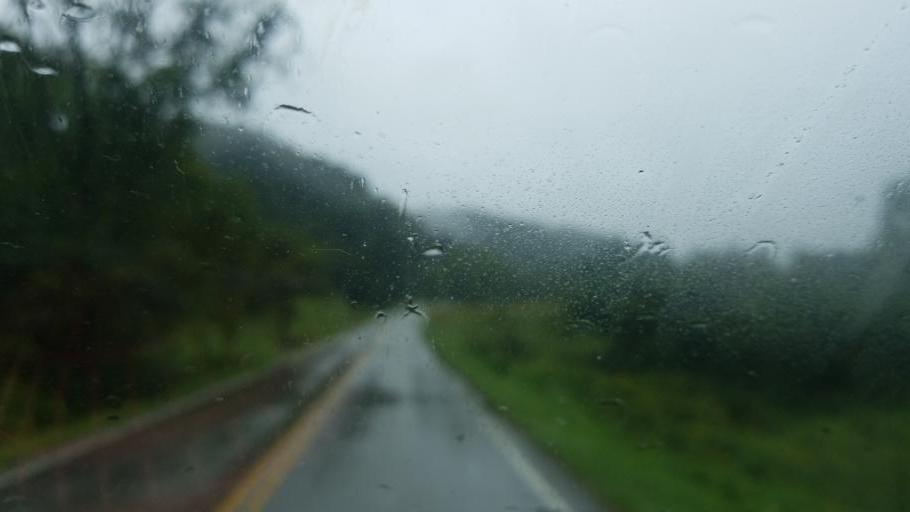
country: US
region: Kentucky
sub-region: Greenup County
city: South Shore
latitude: 38.6916
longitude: -82.9392
